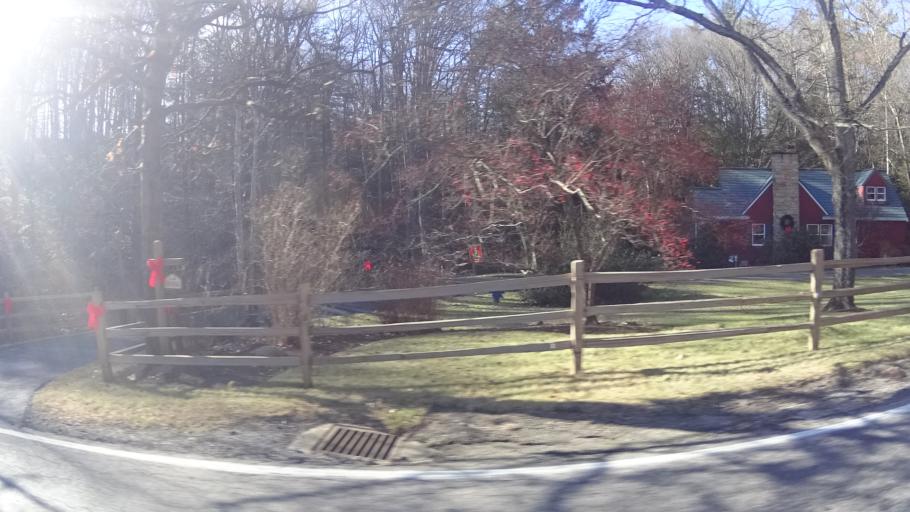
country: US
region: Ohio
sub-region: Lorain County
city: South Amherst
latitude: 41.3599
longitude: -82.3000
